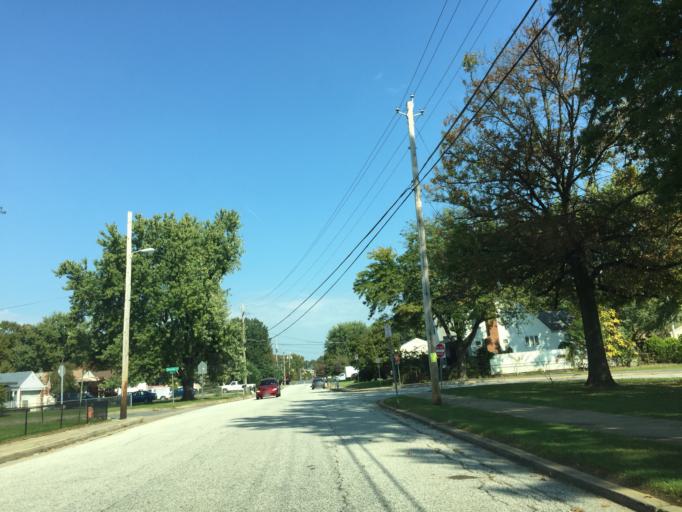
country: US
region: Maryland
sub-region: Baltimore County
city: Essex
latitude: 39.3087
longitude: -76.4553
